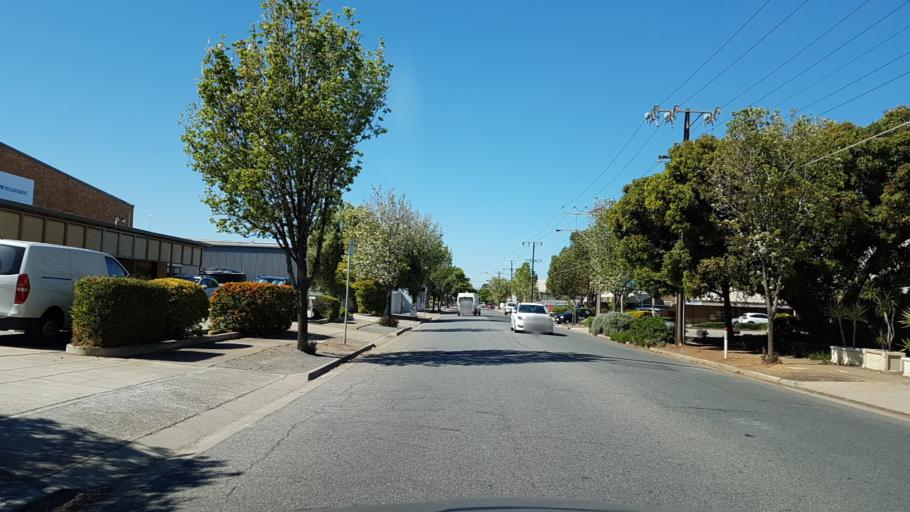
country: AU
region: South Australia
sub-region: City of West Torrens
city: Thebarton
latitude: -34.9168
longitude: 138.5537
